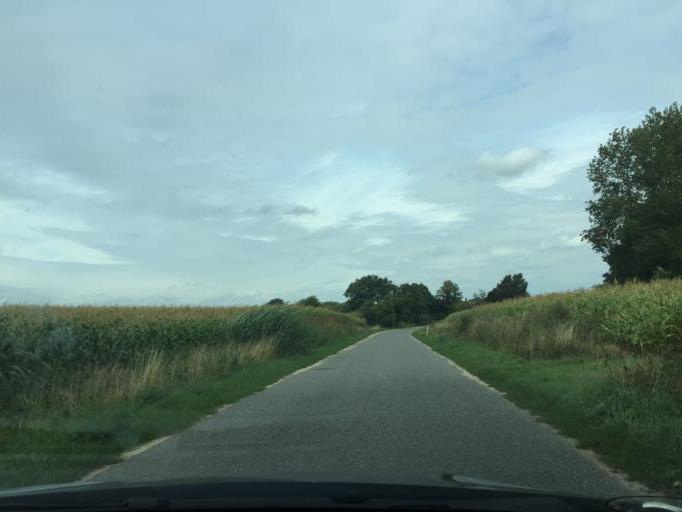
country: DK
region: South Denmark
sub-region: Assens Kommune
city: Vissenbjerg
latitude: 55.3501
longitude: 10.1022
